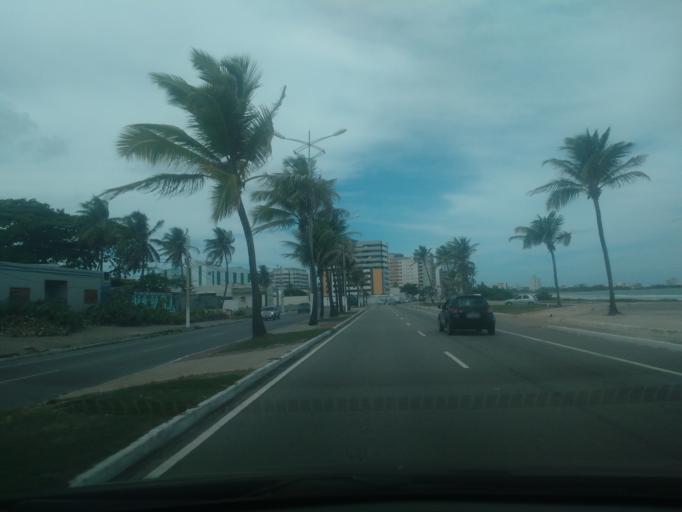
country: BR
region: Alagoas
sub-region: Maceio
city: Maceio
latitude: -9.6712
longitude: -35.7433
